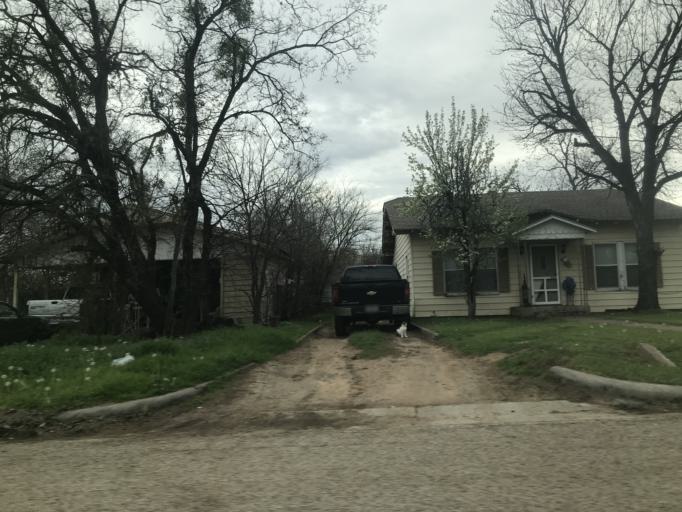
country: US
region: Texas
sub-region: Taylor County
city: Abilene
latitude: 32.4671
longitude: -99.7385
